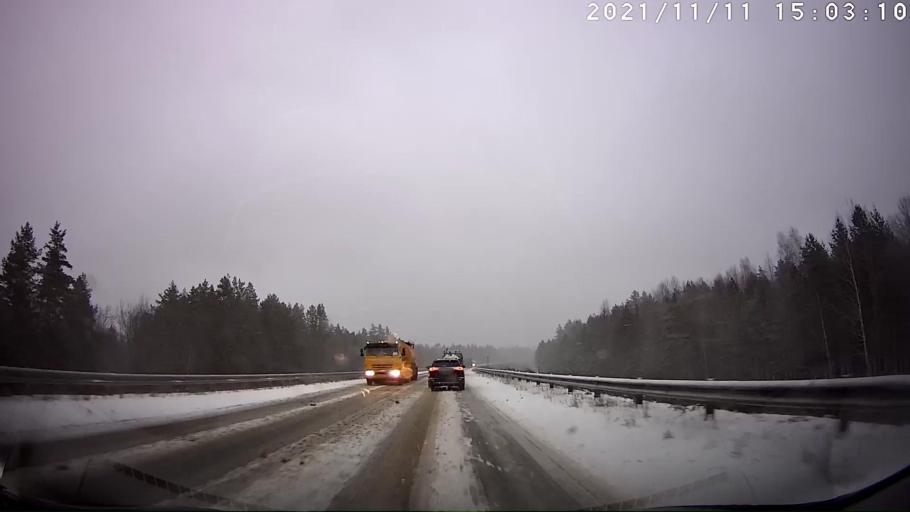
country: RU
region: Chuvashia
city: Mariinskiy Posad
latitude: 56.1943
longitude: 47.7121
